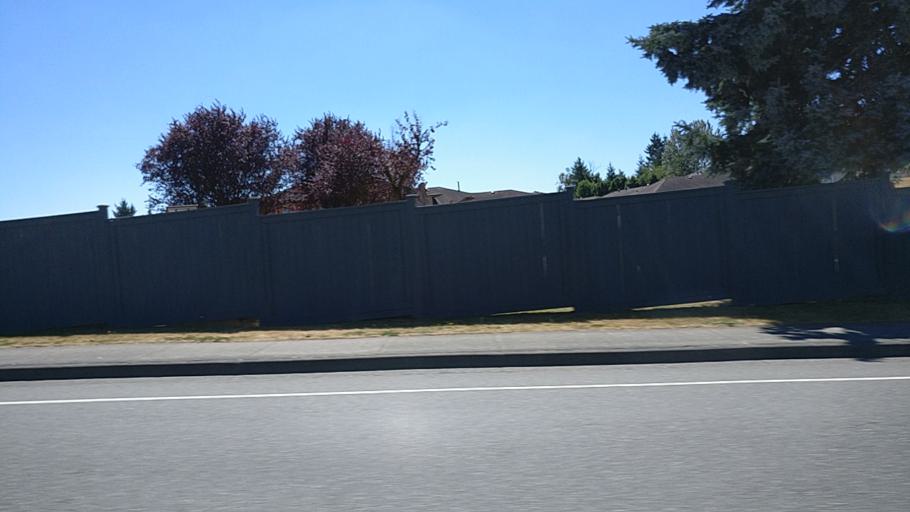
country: CA
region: British Columbia
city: Abbotsford
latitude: 49.0600
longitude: -122.2730
